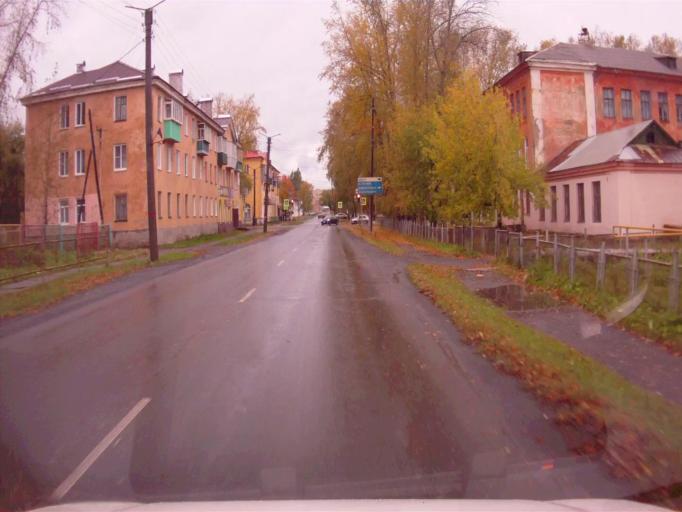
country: RU
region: Chelyabinsk
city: Verkhniy Ufaley
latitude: 56.0341
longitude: 60.2634
